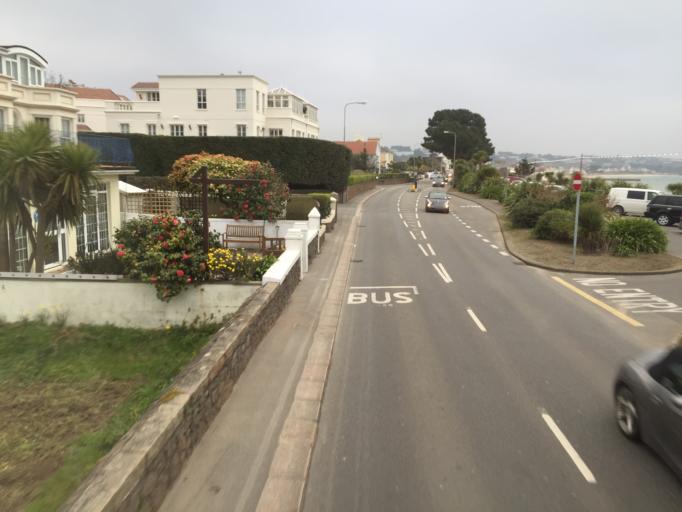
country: JE
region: St Helier
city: Saint Helier
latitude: 49.1940
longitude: -2.1643
